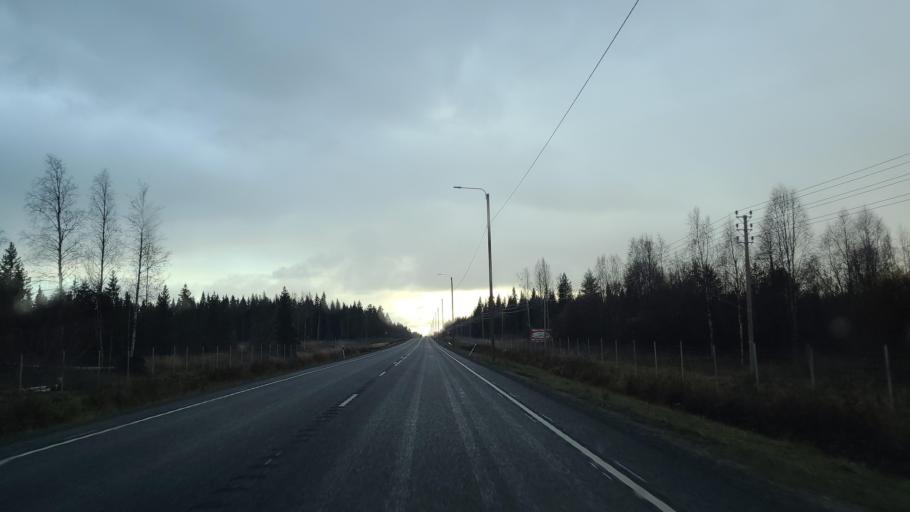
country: FI
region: Northern Ostrobothnia
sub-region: Oulunkaari
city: Ii
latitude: 65.3634
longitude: 25.3734
